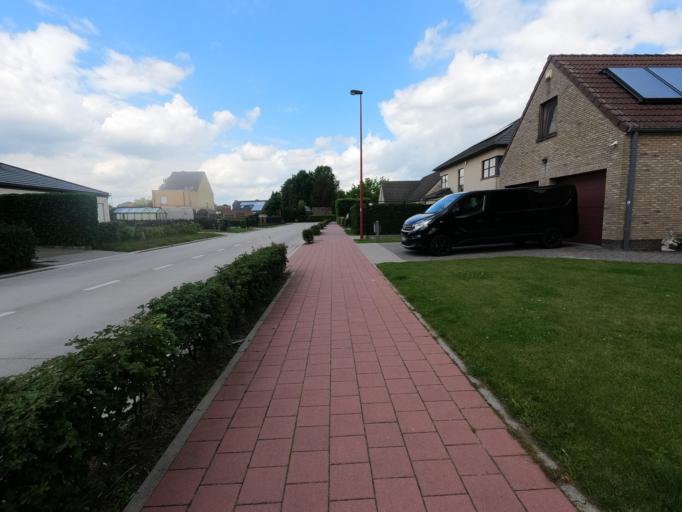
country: BE
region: Flanders
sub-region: Provincie Antwerpen
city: Kalmthout
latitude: 51.3956
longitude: 4.5076
